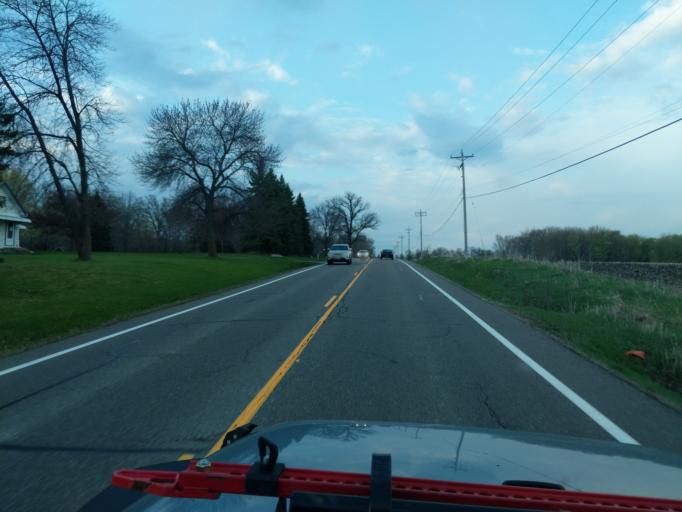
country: US
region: Minnesota
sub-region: Hennepin County
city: Rogers
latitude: 45.1494
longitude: -93.5220
